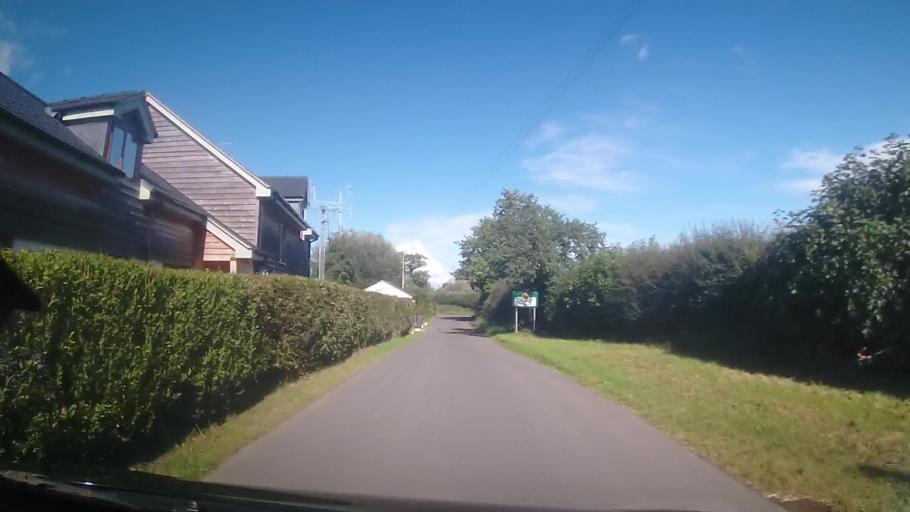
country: GB
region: England
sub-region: Shropshire
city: Wem
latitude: 52.8516
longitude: -2.7015
